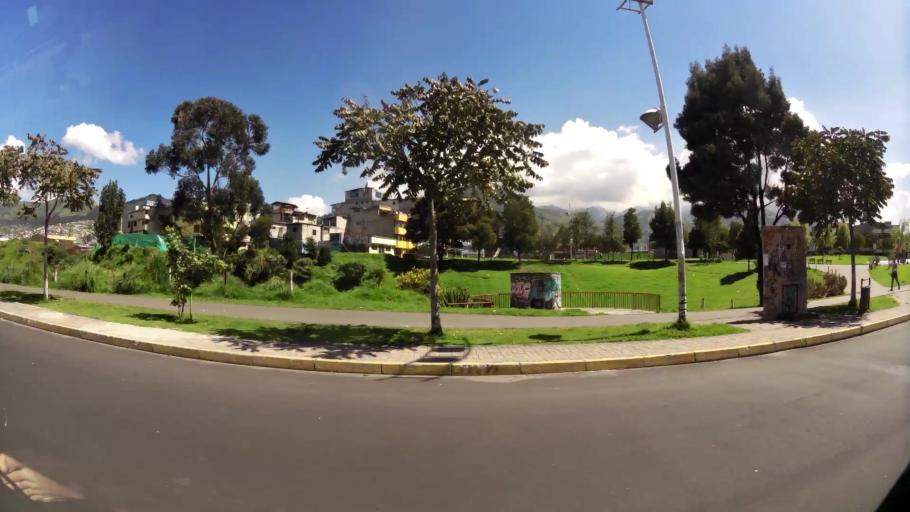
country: EC
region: Pichincha
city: Quito
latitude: -0.2636
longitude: -78.5392
